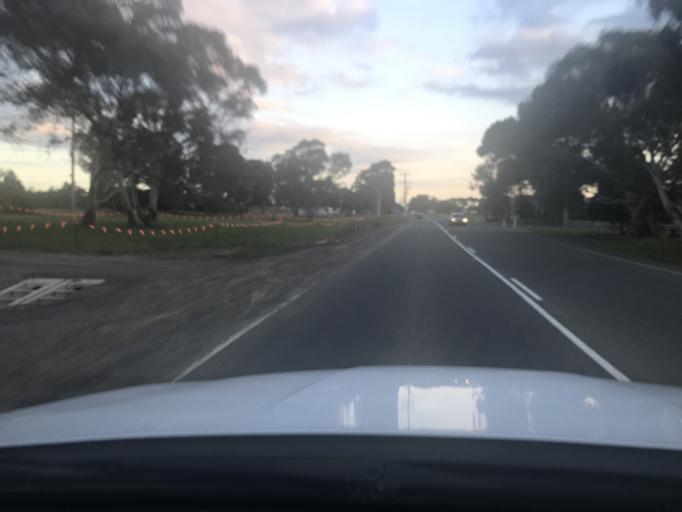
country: AU
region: Victoria
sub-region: Hume
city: Greenvale
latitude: -37.6038
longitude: 144.8831
